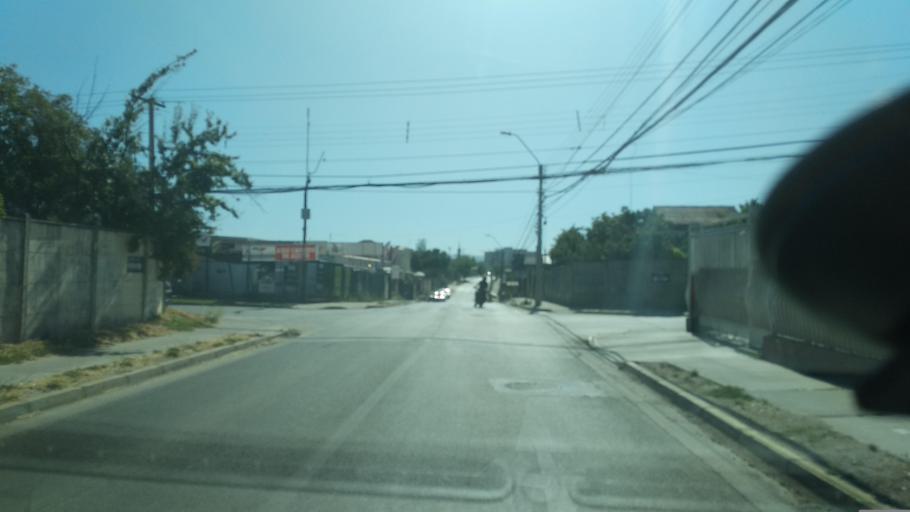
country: CL
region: Valparaiso
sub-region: Provincia de Marga Marga
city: Villa Alemana
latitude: -33.0438
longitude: -71.3881
